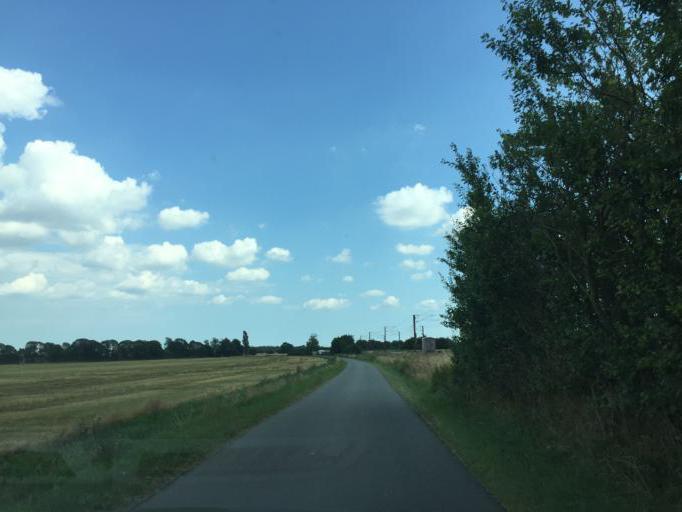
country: DK
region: South Denmark
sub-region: Kerteminde Kommune
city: Langeskov
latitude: 55.3756
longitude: 10.5353
